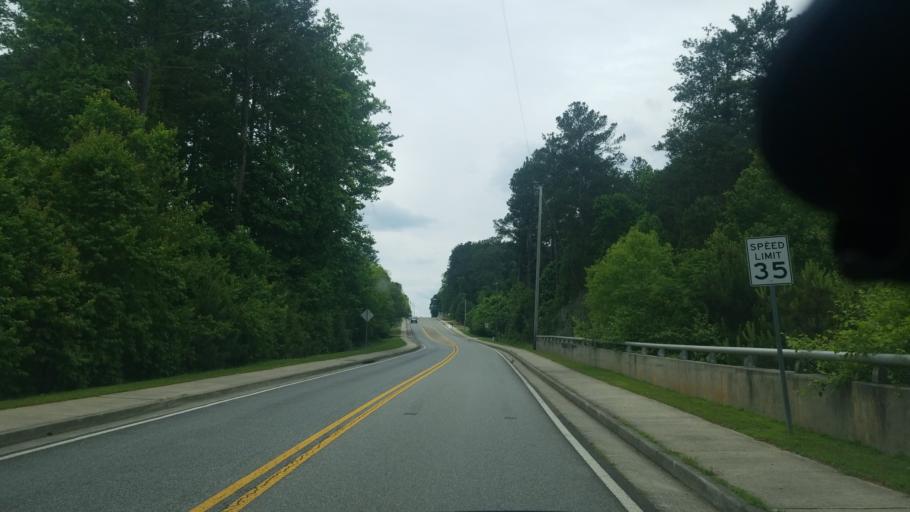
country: US
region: Georgia
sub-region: Forsyth County
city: Cumming
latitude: 34.1943
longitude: -84.1068
